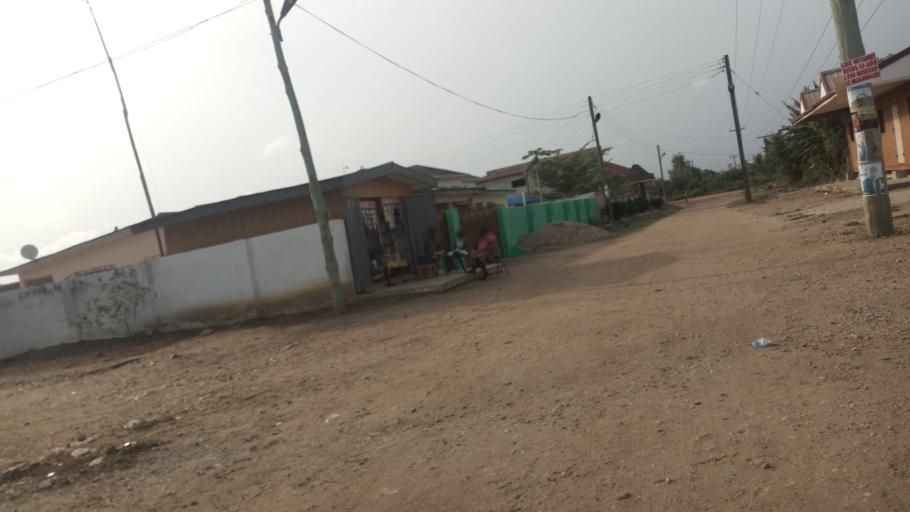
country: GH
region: Central
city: Winneba
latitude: 5.3536
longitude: -0.6329
